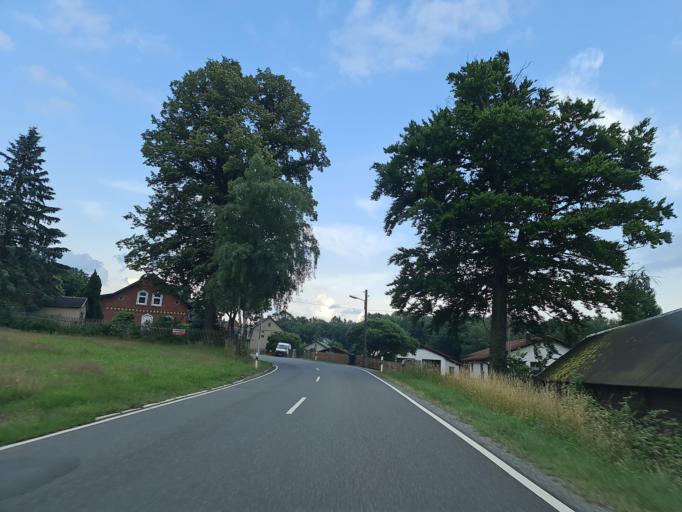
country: DE
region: Saxony
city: Bergen
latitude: 50.4641
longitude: 12.2827
